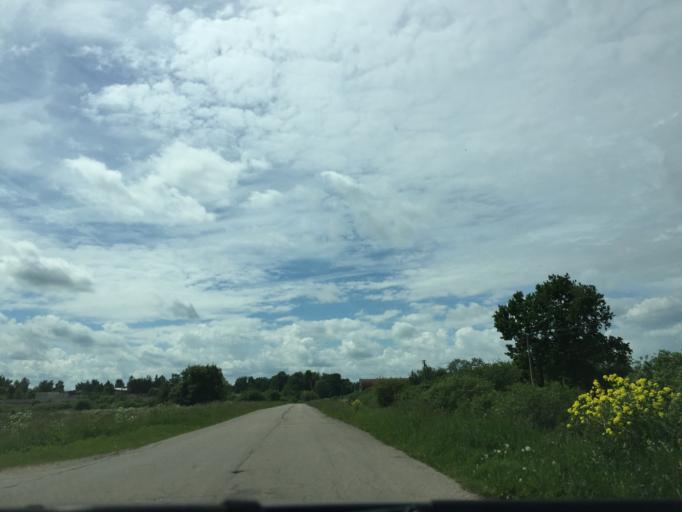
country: LV
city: Tireli
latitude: 56.6899
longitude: 23.5086
